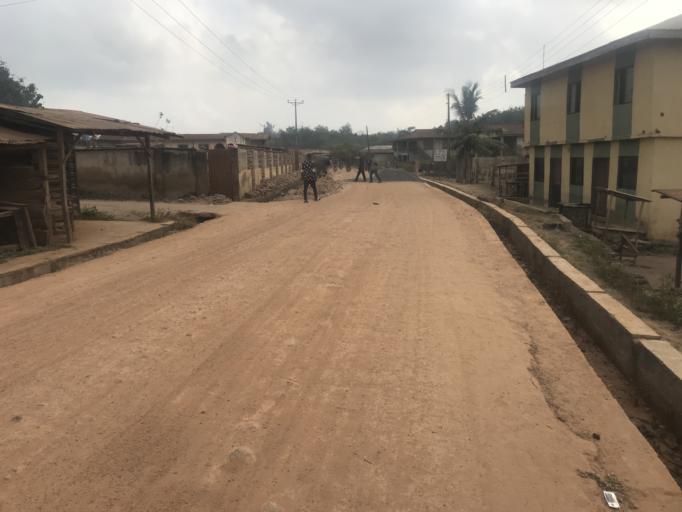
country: NG
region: Osun
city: Ikire
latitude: 7.3707
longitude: 4.1986
